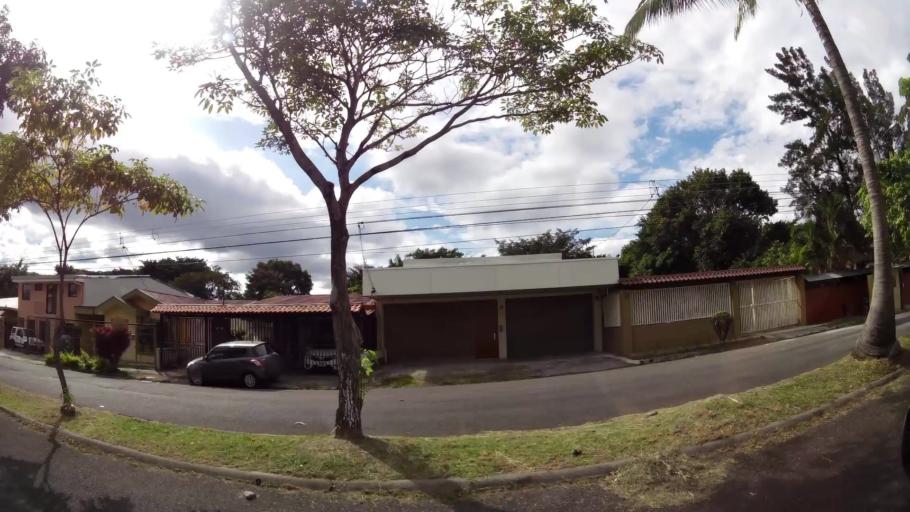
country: CR
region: San Jose
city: San Rafael
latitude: 9.9530
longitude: -84.1284
